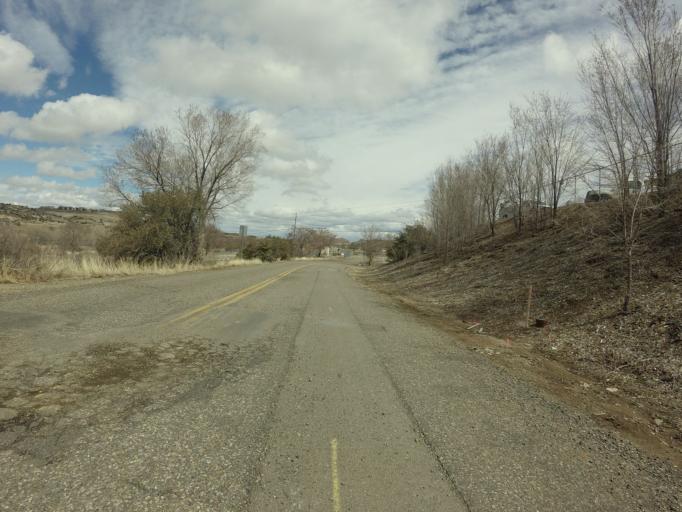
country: US
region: Arizona
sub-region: Yavapai County
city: Prescott
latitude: 34.5689
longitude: -112.4337
